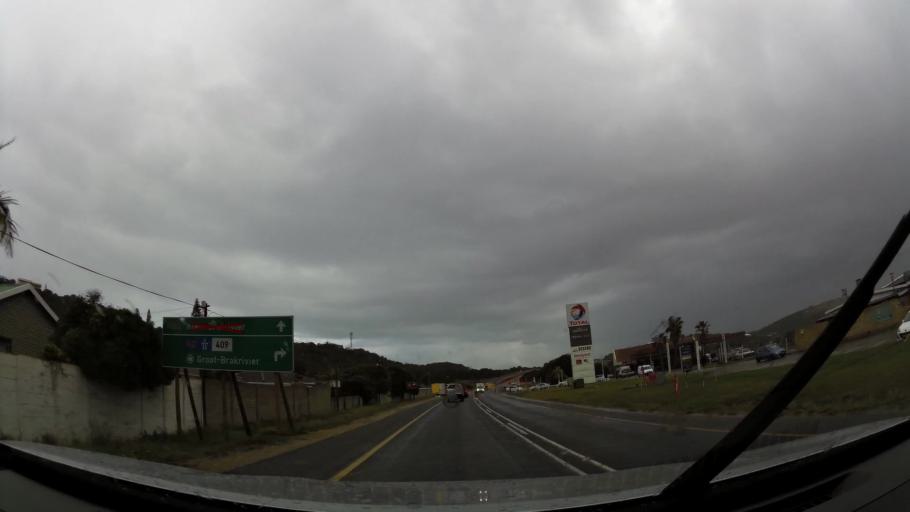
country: ZA
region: Western Cape
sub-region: Eden District Municipality
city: Mossel Bay
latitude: -34.0548
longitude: 22.2255
